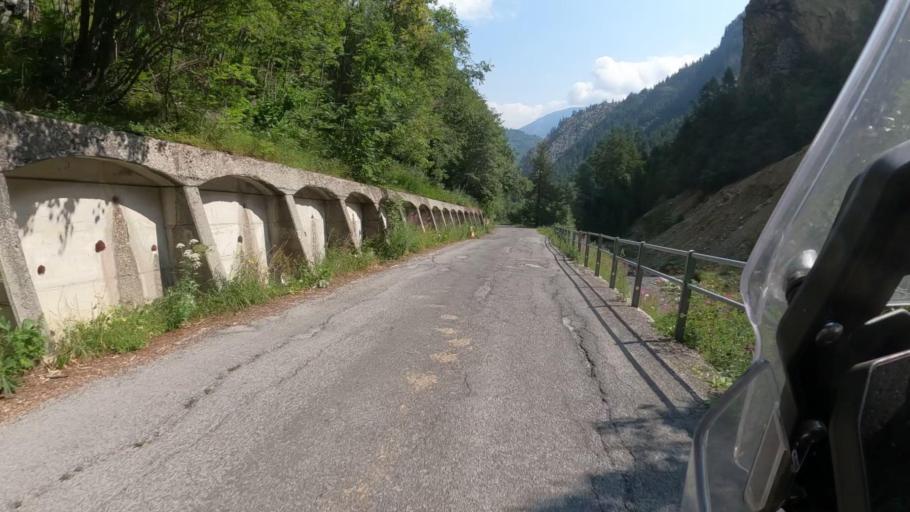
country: IT
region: Piedmont
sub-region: Provincia di Cuneo
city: Canosio
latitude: 44.4433
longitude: 7.0639
